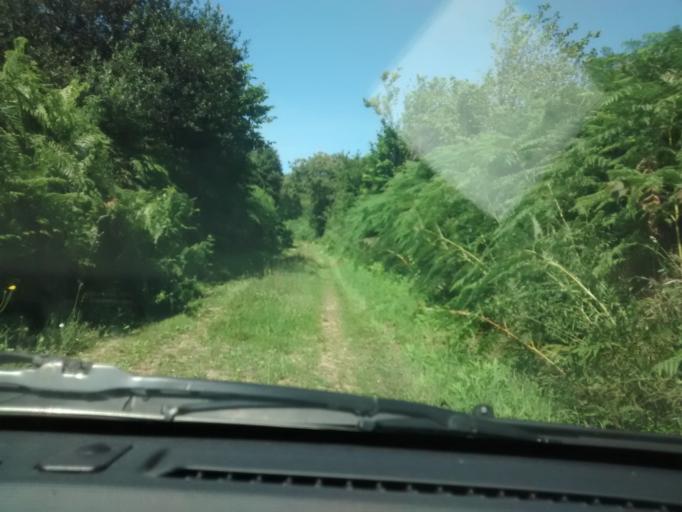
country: FR
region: Brittany
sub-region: Departement des Cotes-d'Armor
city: Trevou-Treguignec
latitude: 48.7771
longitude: -3.3366
